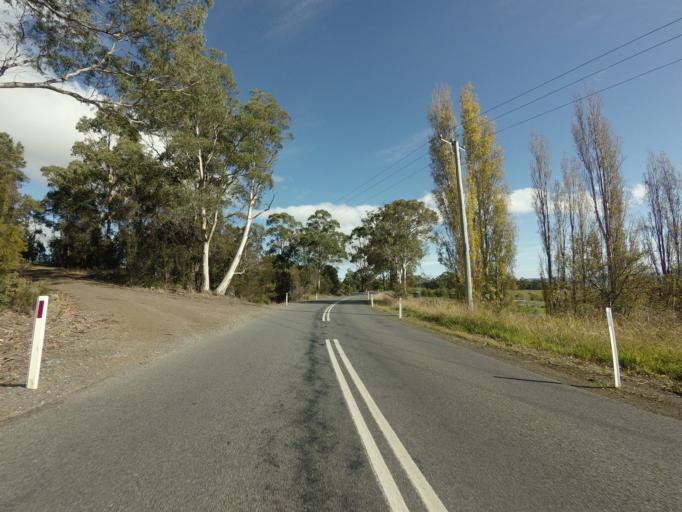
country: AU
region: Tasmania
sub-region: Clarence
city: Sandford
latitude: -43.0615
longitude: 147.8275
